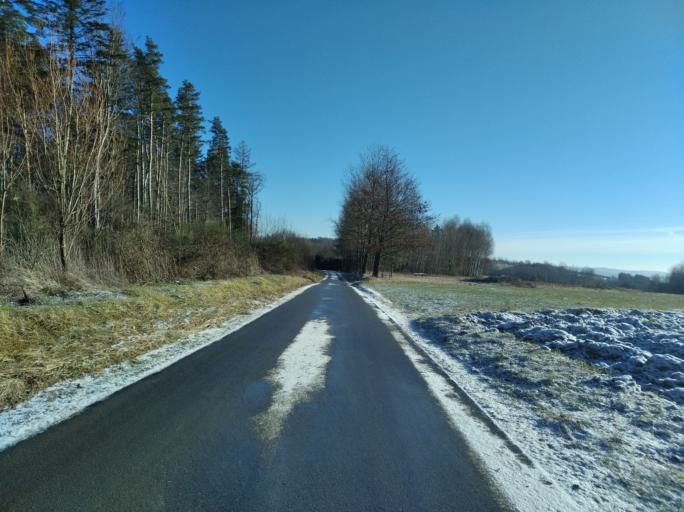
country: PL
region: Subcarpathian Voivodeship
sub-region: Powiat strzyzowski
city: Czudec
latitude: 49.9714
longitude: 21.8062
